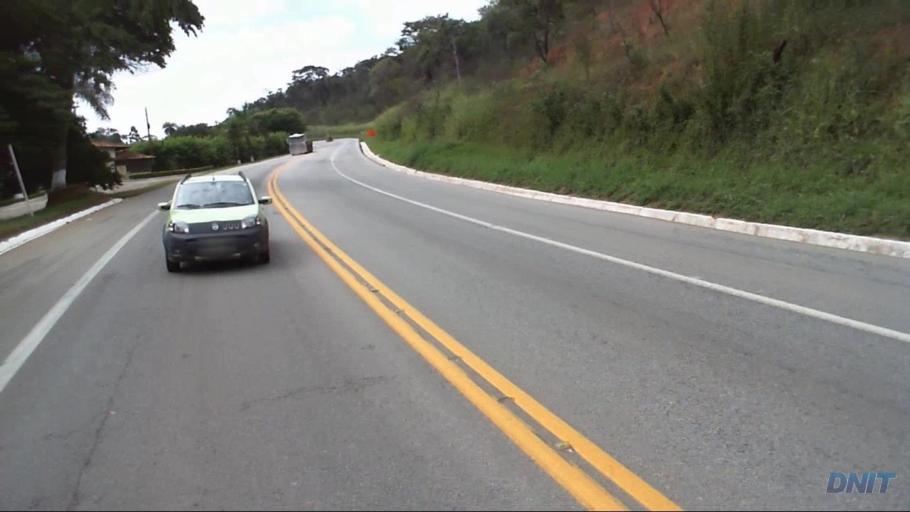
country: BR
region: Minas Gerais
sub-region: Caete
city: Caete
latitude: -19.7664
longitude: -43.6443
